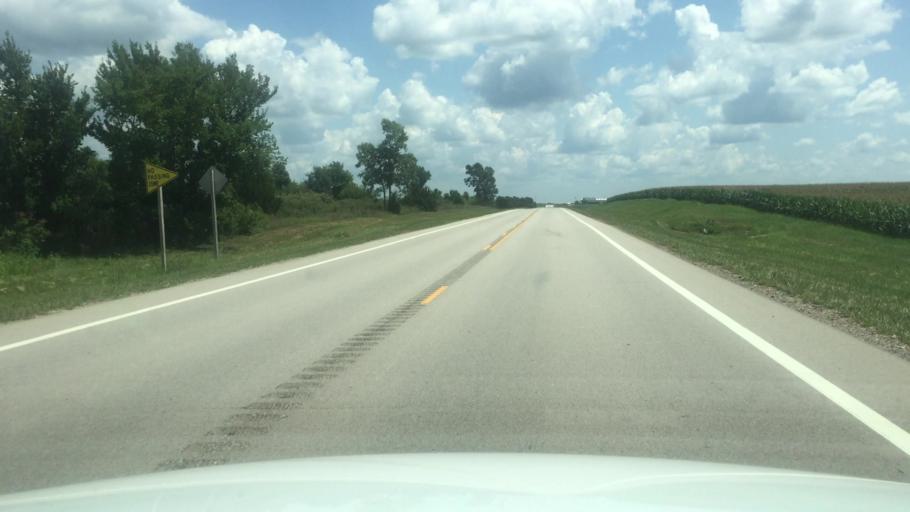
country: US
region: Kansas
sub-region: Brown County
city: Horton
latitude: 39.6574
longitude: -95.3750
